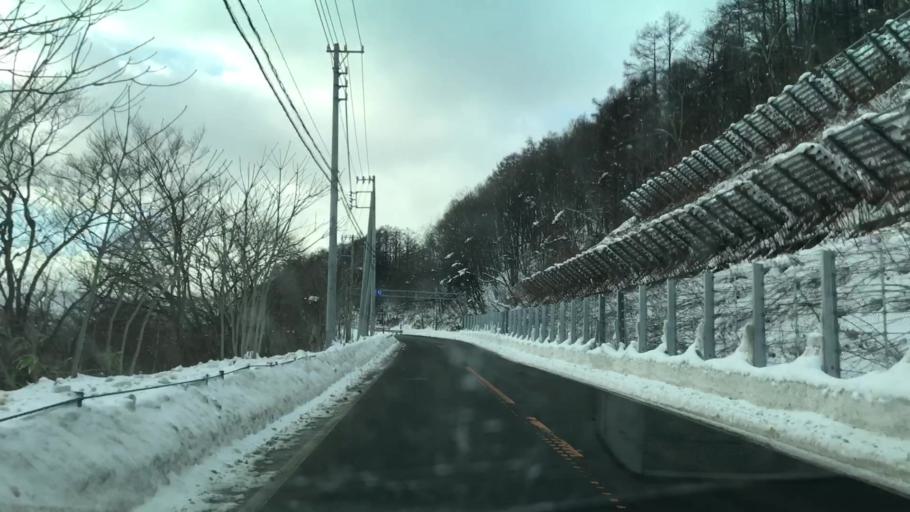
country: JP
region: Hokkaido
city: Yoichi
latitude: 43.2924
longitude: 140.5915
